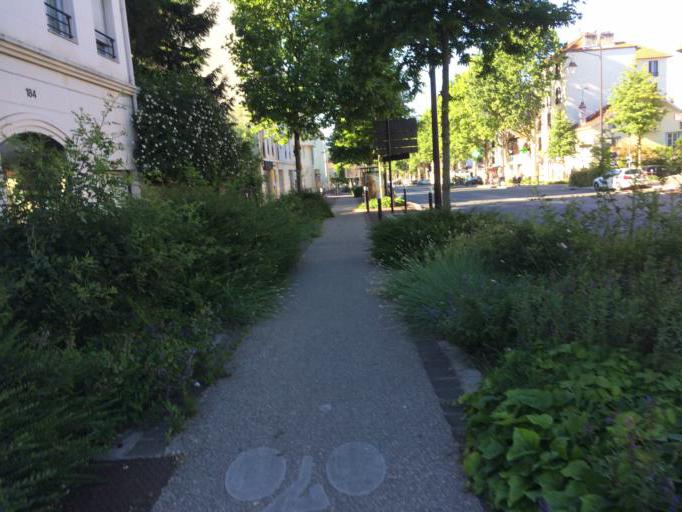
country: FR
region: Ile-de-France
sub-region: Departement des Hauts-de-Seine
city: Antony
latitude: 48.7409
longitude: 2.3023
